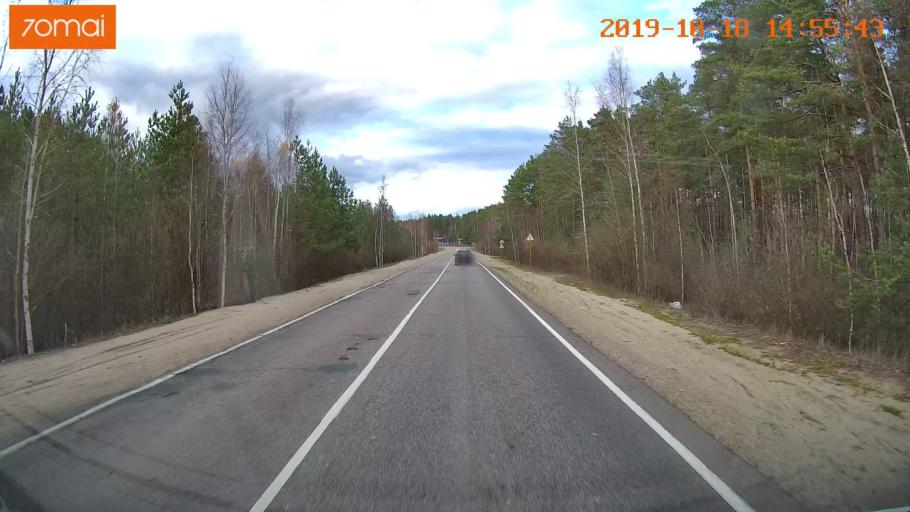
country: RU
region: Vladimir
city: Kurlovo
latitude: 55.4561
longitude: 40.5898
